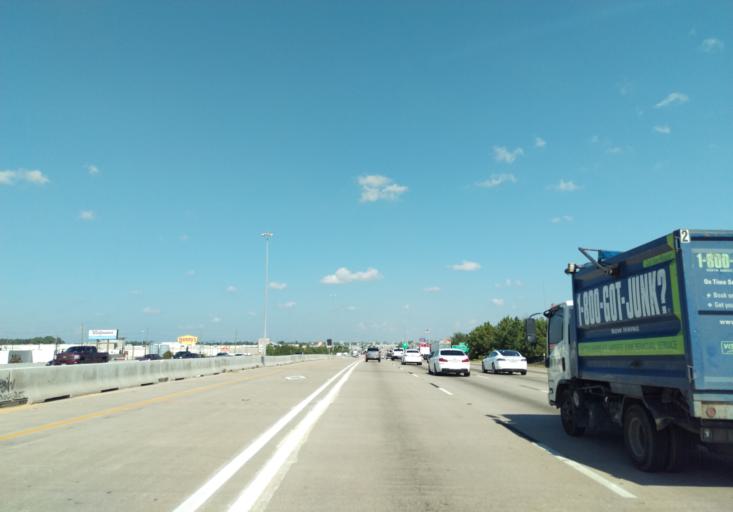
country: US
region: Texas
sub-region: Harris County
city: Spring
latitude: 30.0525
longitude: -95.4317
